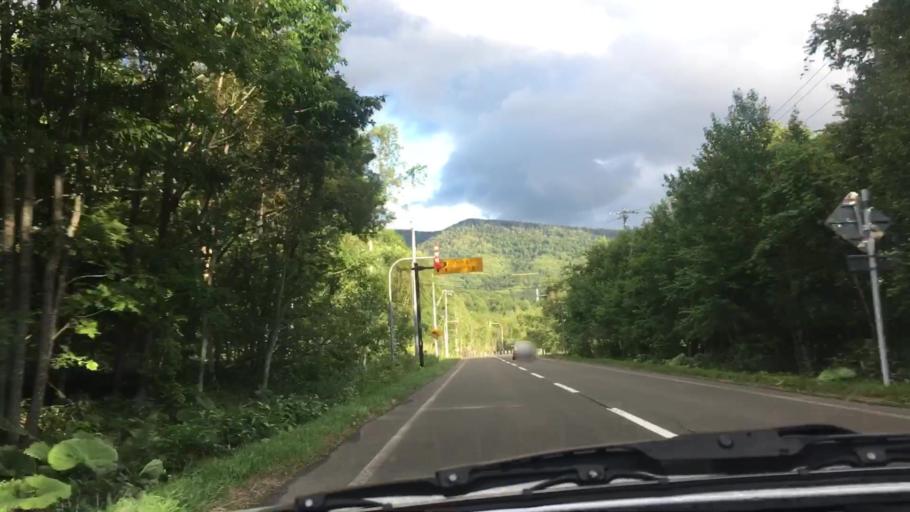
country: JP
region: Hokkaido
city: Shimo-furano
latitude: 43.1151
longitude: 142.6844
